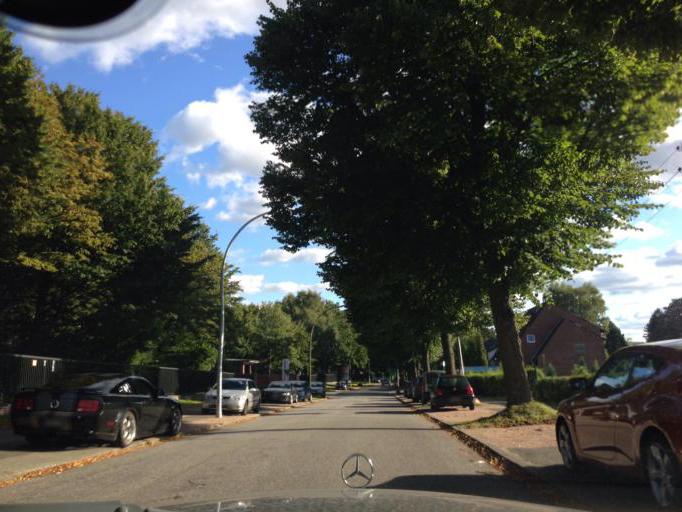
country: DE
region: Hamburg
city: Wandsbek
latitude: 53.5633
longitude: 10.0948
